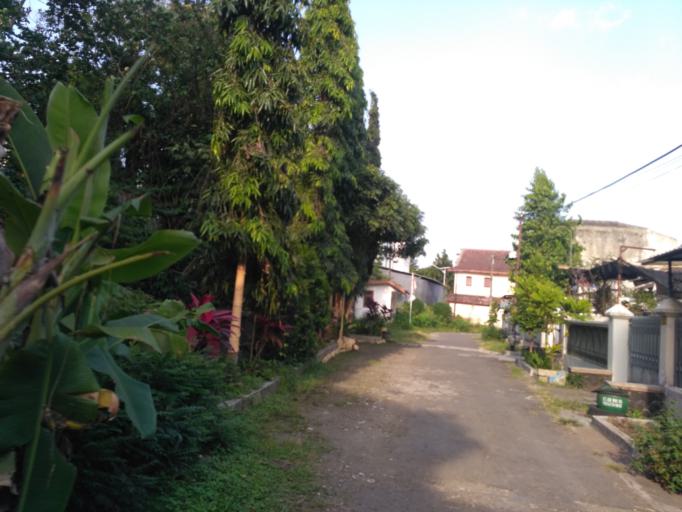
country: ID
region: East Java
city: Malang
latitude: -7.9370
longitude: 112.6319
